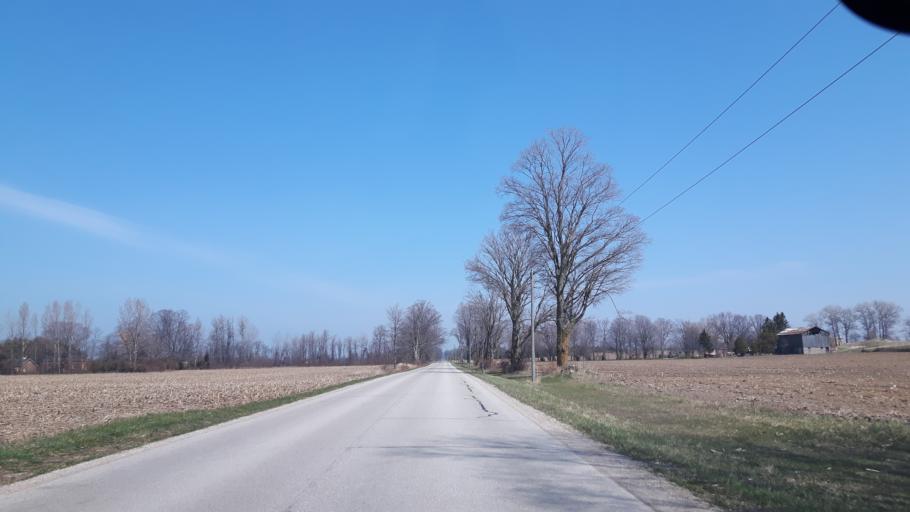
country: CA
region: Ontario
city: Goderich
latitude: 43.6761
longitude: -81.6847
